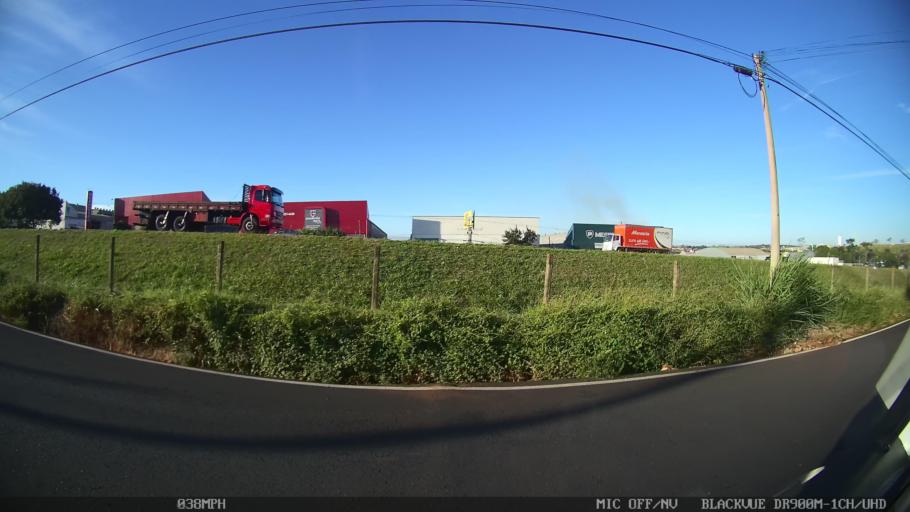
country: BR
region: Sao Paulo
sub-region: Sao Jose Do Rio Preto
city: Sao Jose do Rio Preto
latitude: -20.8587
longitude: -49.3373
